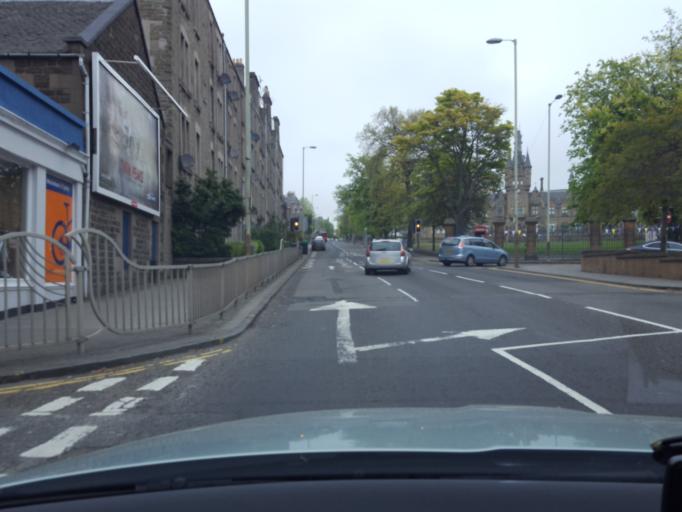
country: GB
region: Scotland
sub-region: Dundee City
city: Dundee
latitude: 56.4729
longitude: -2.9564
